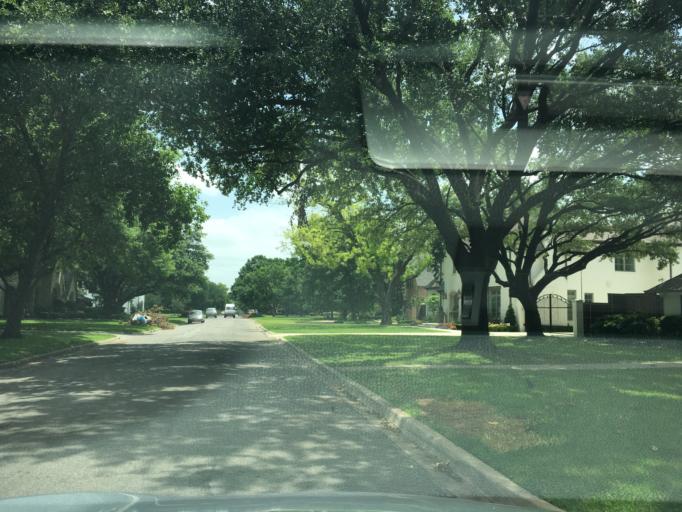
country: US
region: Texas
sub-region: Dallas County
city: University Park
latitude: 32.8915
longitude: -96.7921
